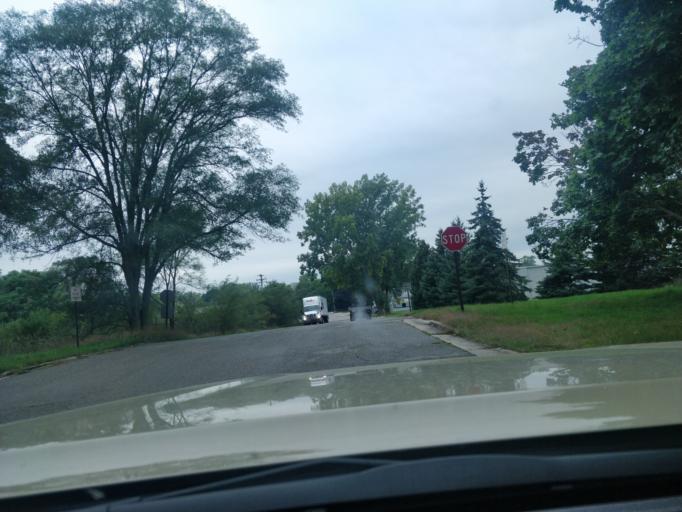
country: US
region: Michigan
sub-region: Kent County
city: Wyoming
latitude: 42.9175
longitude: -85.7266
